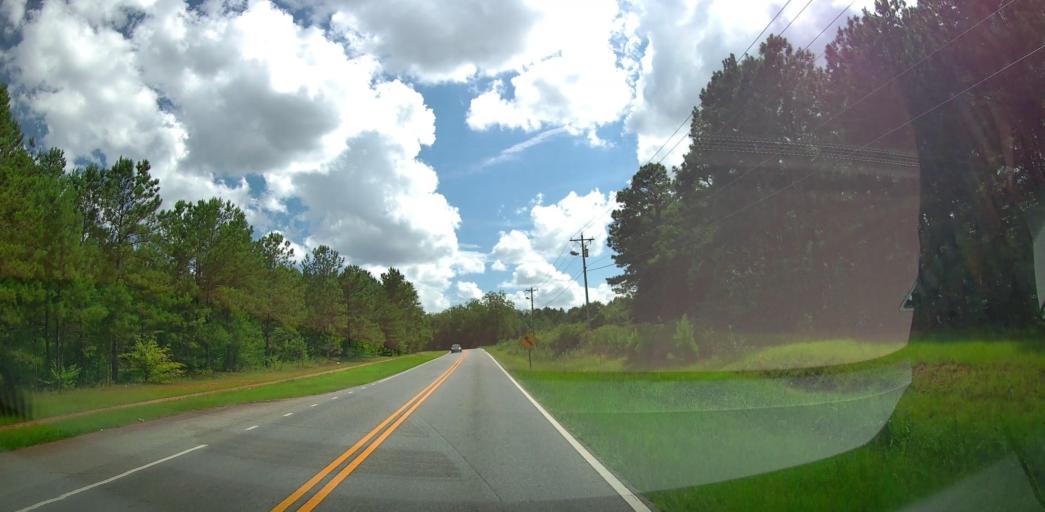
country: US
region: Georgia
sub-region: Houston County
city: Warner Robins
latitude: 32.6485
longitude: -83.6280
